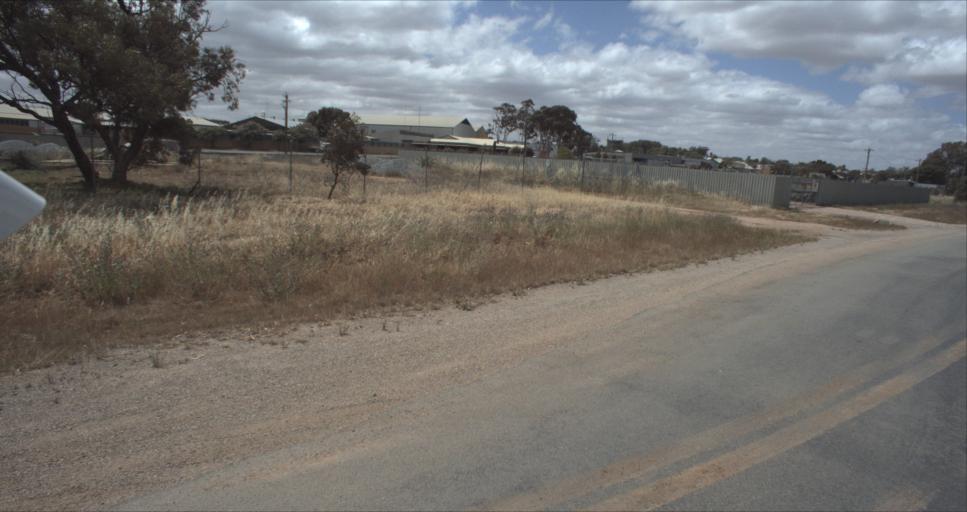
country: AU
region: New South Wales
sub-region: Leeton
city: Leeton
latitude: -34.5530
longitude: 146.3938
